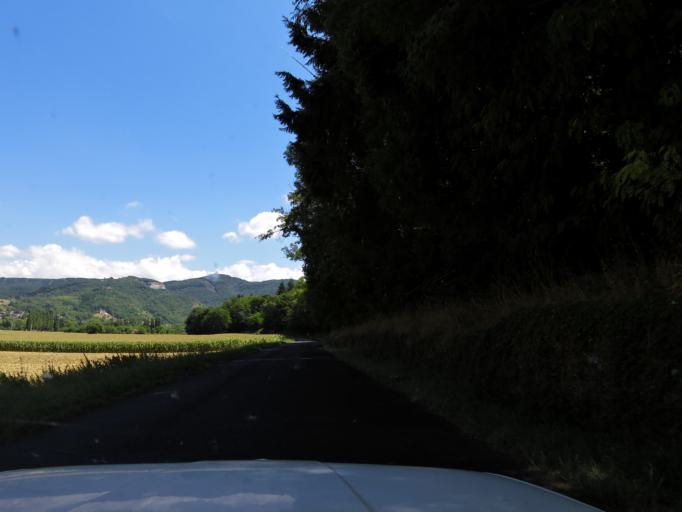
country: FR
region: Rhone-Alpes
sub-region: Departement de l'Ain
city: Amberieu-en-Bugey
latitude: 45.9468
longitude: 5.3437
